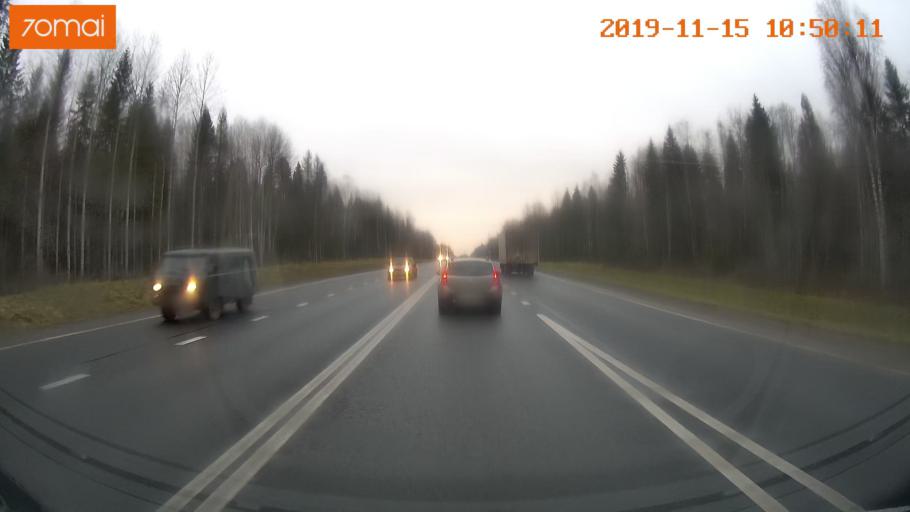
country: RU
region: Vologda
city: Chebsara
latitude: 59.1868
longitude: 38.6746
